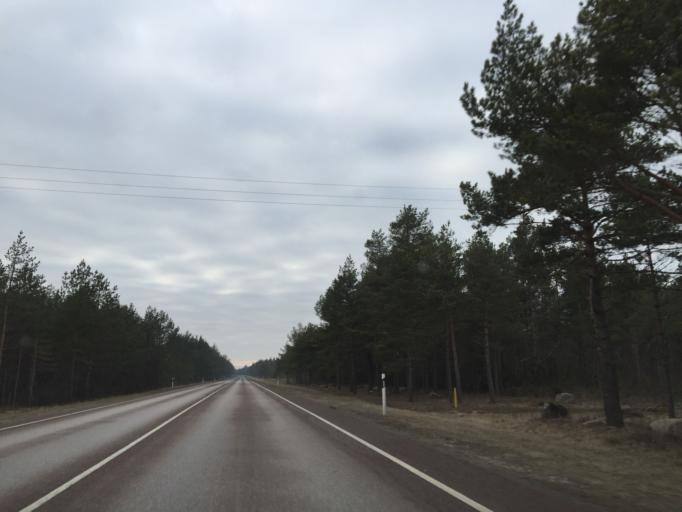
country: EE
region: Saare
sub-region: Orissaare vald
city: Orissaare
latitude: 58.5306
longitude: 22.9898
